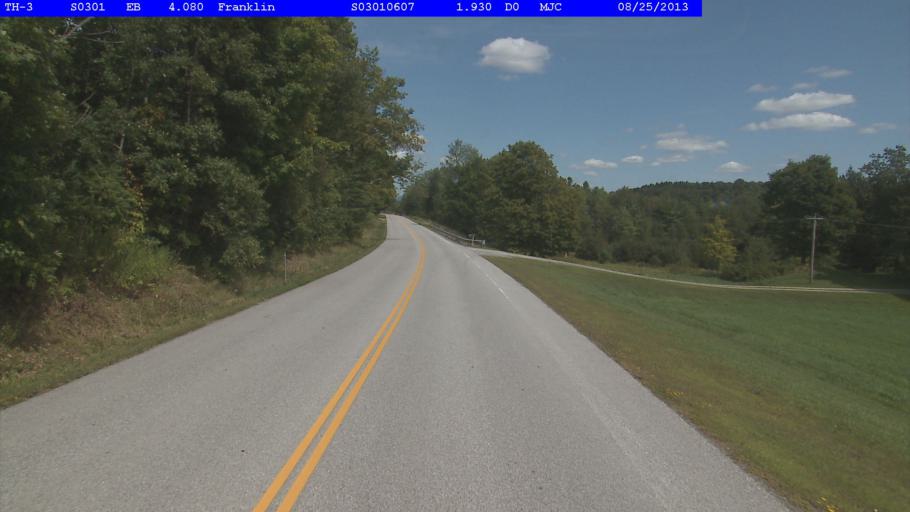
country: CA
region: Quebec
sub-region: Monteregie
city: Bedford
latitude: 44.9737
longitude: -72.9461
